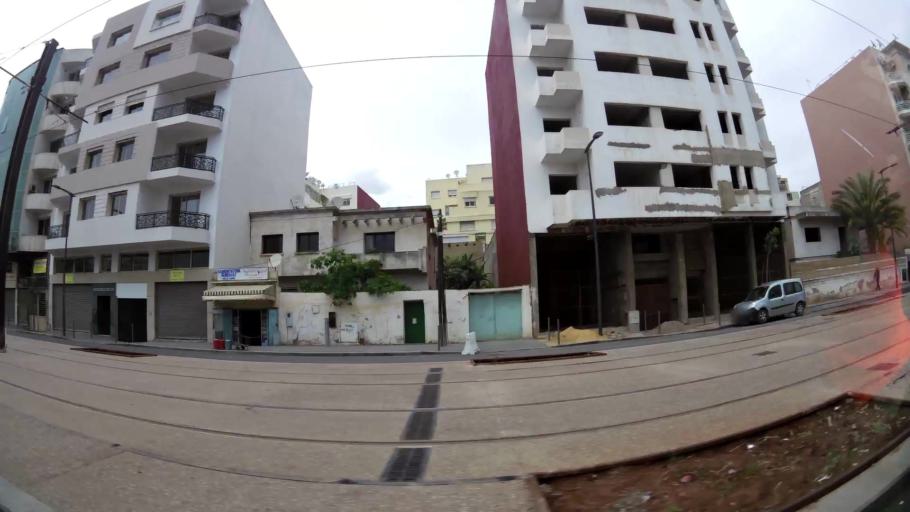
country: MA
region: Grand Casablanca
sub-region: Casablanca
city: Casablanca
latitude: 33.5695
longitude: -7.6232
